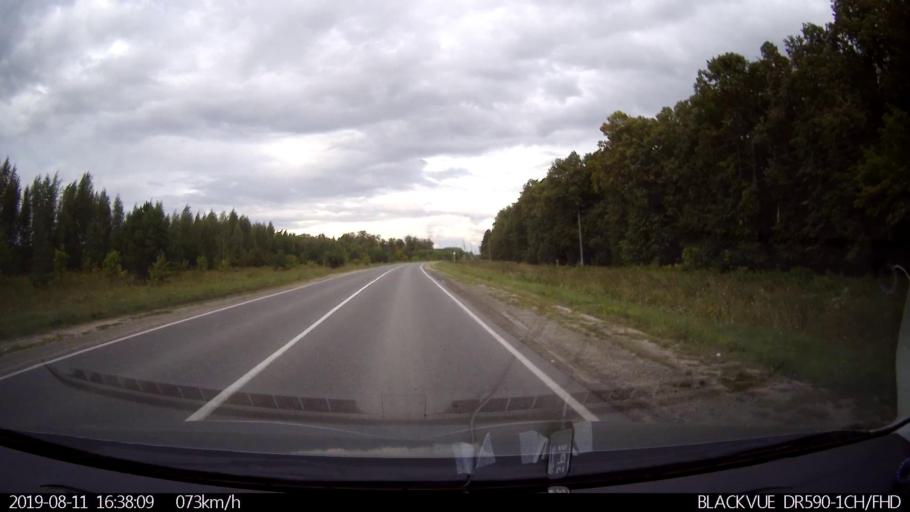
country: RU
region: Ulyanovsk
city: Mayna
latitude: 54.1330
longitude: 47.6216
